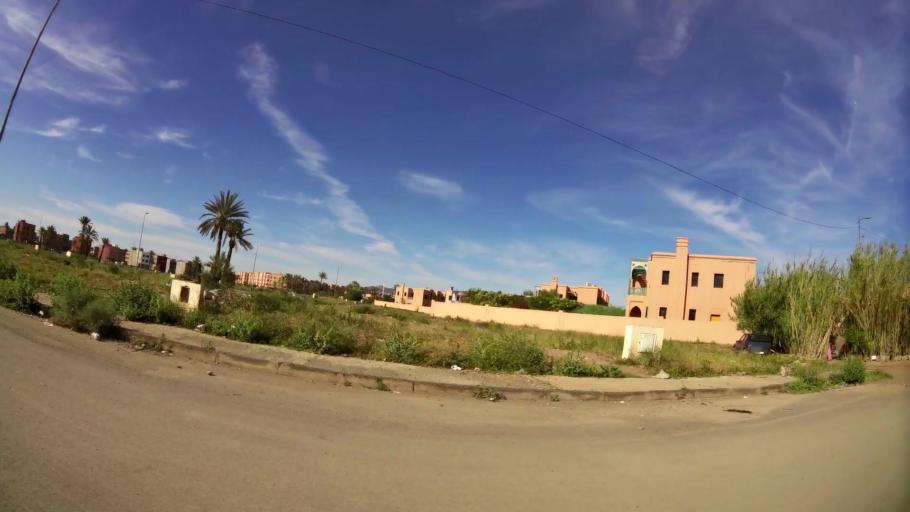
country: MA
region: Marrakech-Tensift-Al Haouz
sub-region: Marrakech
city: Marrakesh
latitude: 31.6750
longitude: -8.0565
